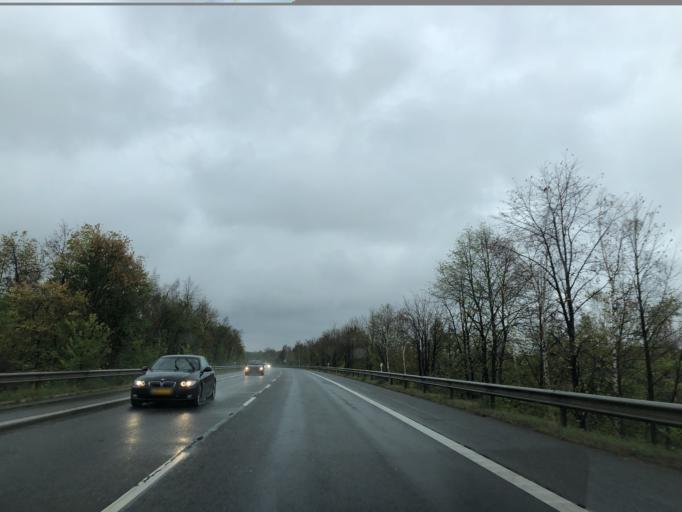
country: DE
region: North Rhine-Westphalia
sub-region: Regierungsbezirk Dusseldorf
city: Grevenbroich
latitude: 51.0437
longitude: 6.5657
